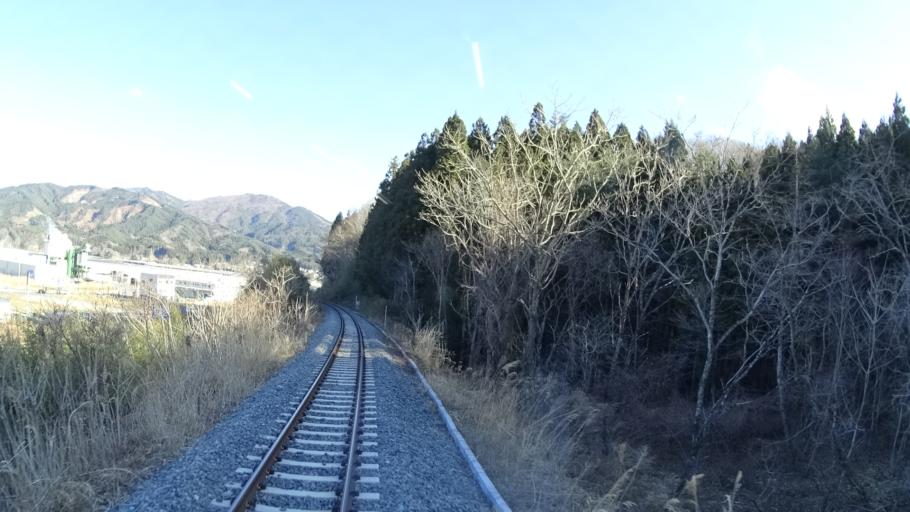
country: JP
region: Iwate
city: Miyako
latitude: 39.5929
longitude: 141.9424
